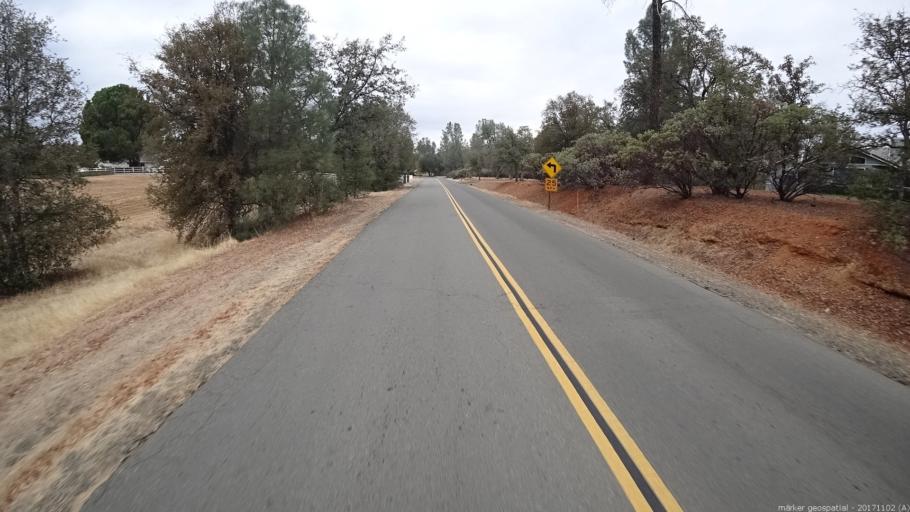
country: US
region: California
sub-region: Shasta County
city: Shasta Lake
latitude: 40.6568
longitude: -122.3189
